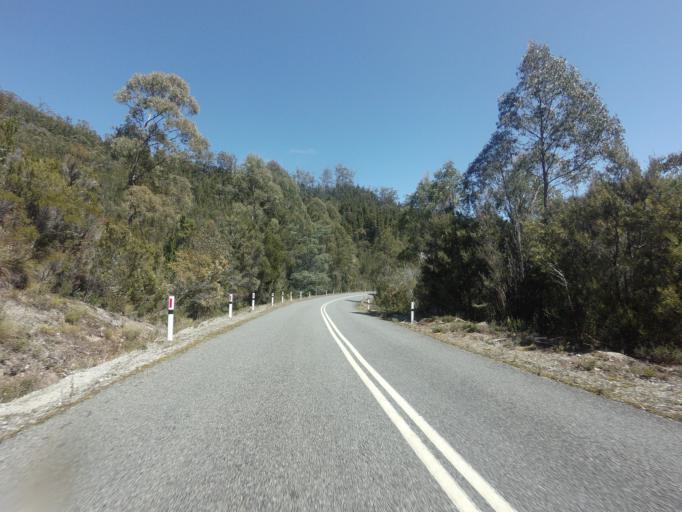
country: AU
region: Tasmania
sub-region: Huon Valley
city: Geeveston
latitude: -42.8158
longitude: 146.3755
